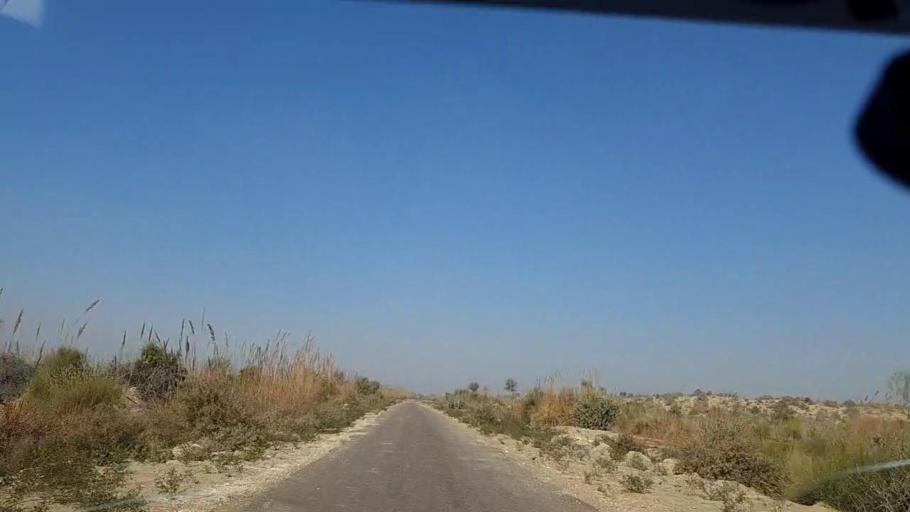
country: PK
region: Sindh
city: Khanpur
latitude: 27.5833
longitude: 69.3764
